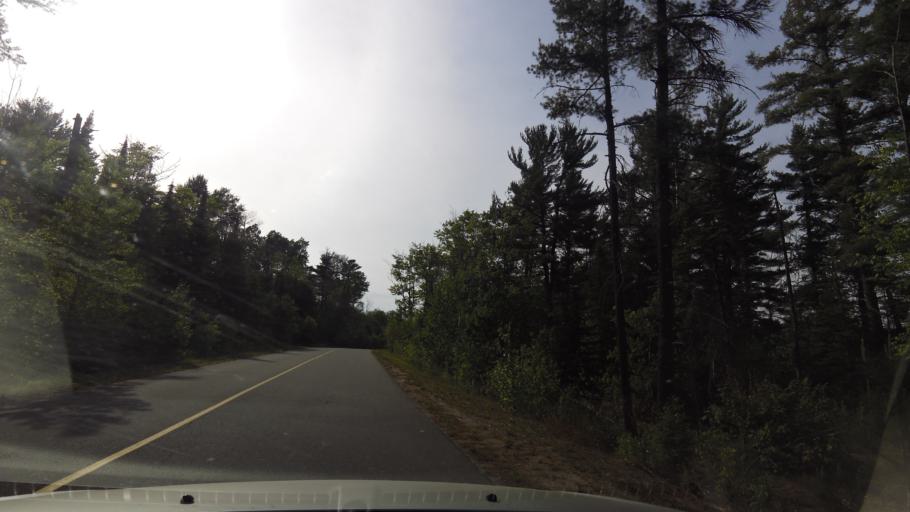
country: CA
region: Ontario
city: Greater Sudbury
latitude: 46.0148
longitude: -80.5825
